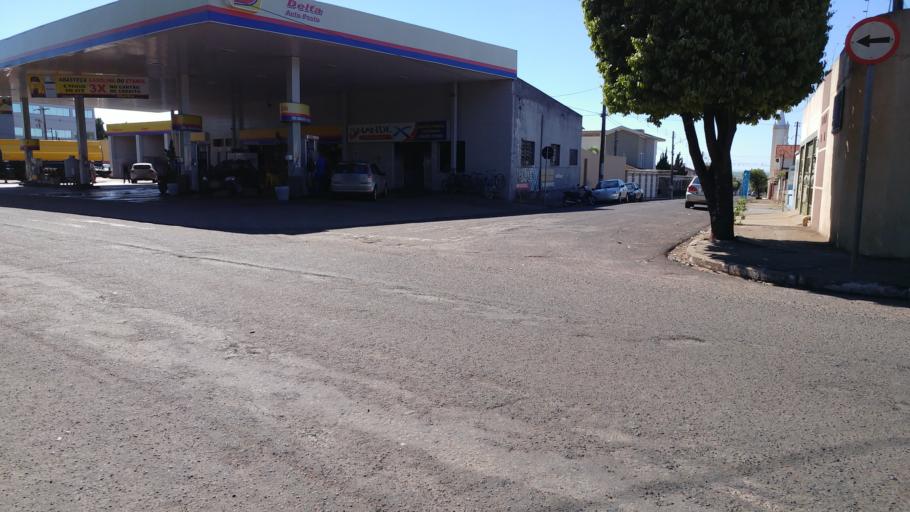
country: BR
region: Sao Paulo
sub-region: Paraguacu Paulista
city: Paraguacu Paulista
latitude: -22.4183
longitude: -50.5789
